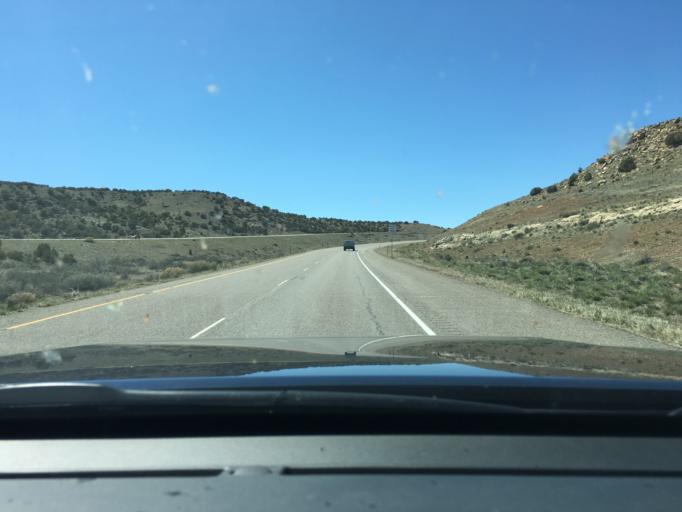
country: US
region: Colorado
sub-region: Mesa County
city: Loma
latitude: 39.1890
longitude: -109.0300
